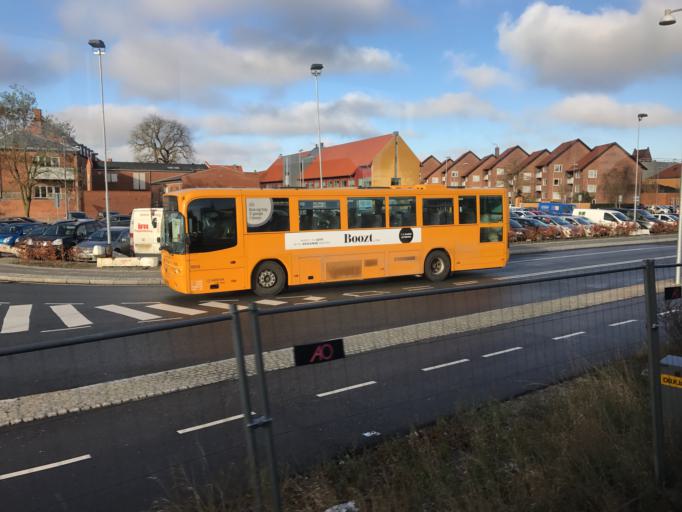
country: DK
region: Zealand
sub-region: Koge Kommune
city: Koge
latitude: 55.4538
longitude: 12.1851
